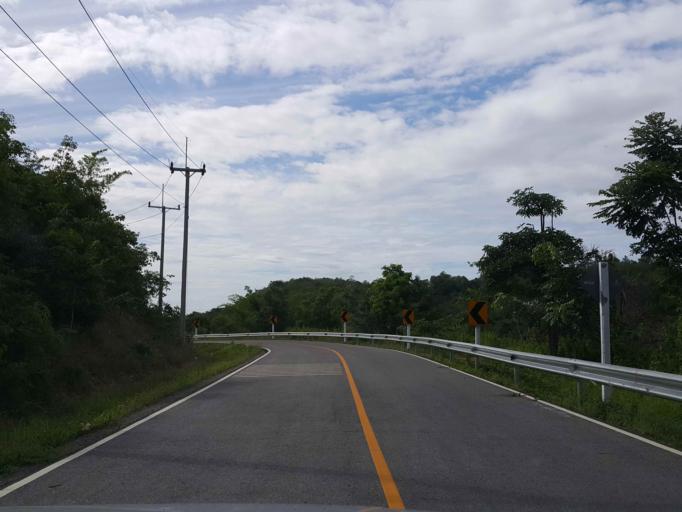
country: TH
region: Sukhothai
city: Thung Saliam
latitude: 17.2400
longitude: 99.4959
